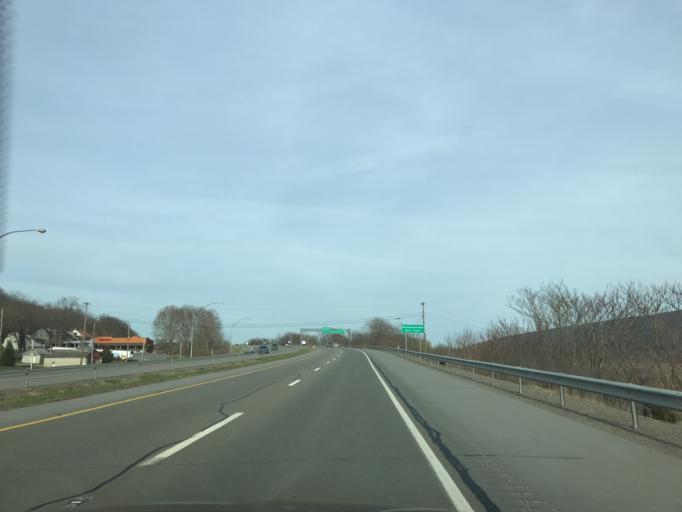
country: US
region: Pennsylvania
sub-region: Lycoming County
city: Kenmar
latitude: 41.2456
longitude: -76.9544
